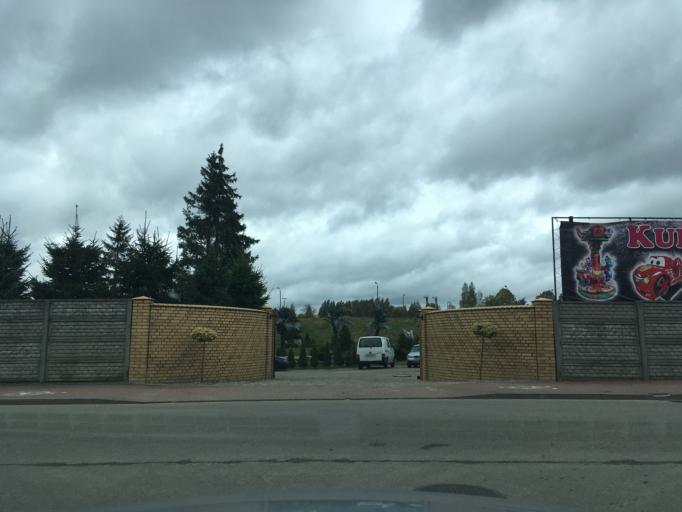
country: PL
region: Pomeranian Voivodeship
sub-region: Powiat koscierski
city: Koscierzyna
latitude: 54.1155
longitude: 18.0006
